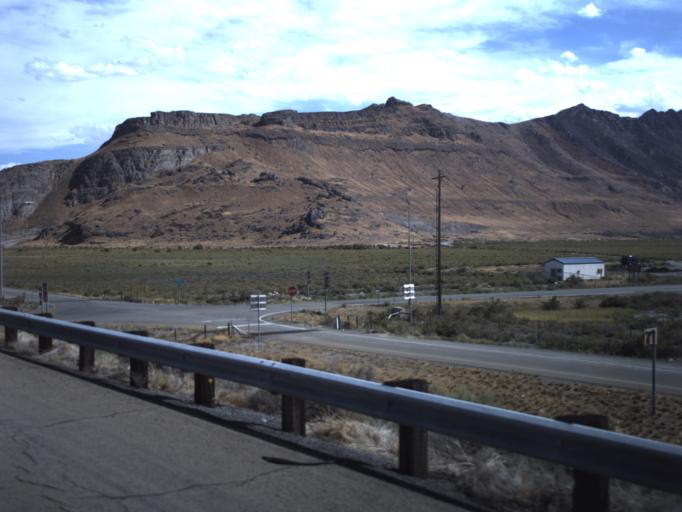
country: US
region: Utah
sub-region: Tooele County
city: Grantsville
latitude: 40.7457
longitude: -112.6540
